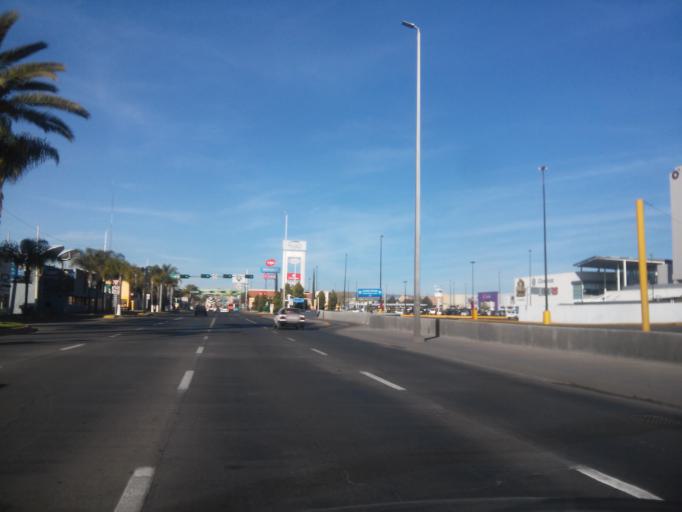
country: MX
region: Durango
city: Victoria de Durango
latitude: 24.0345
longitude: -104.6502
